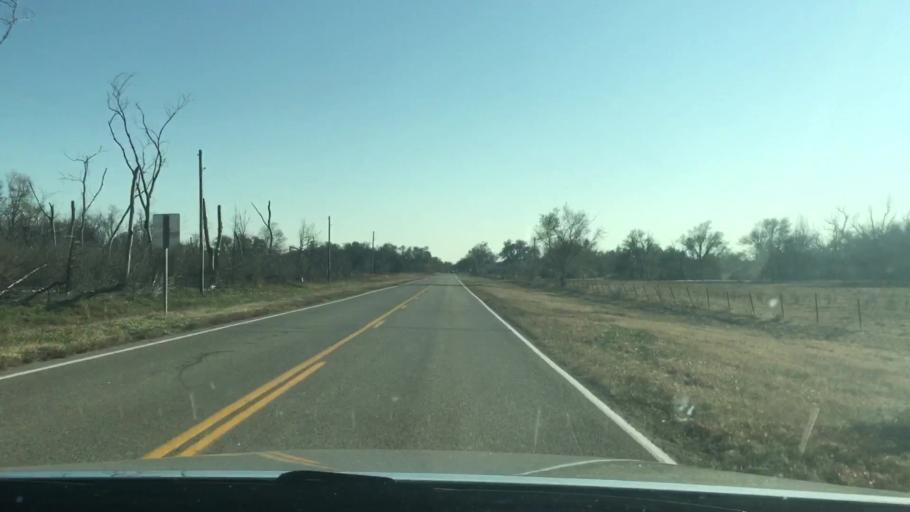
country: US
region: Kansas
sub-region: Reno County
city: Nickerson
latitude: 38.1608
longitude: -98.0875
